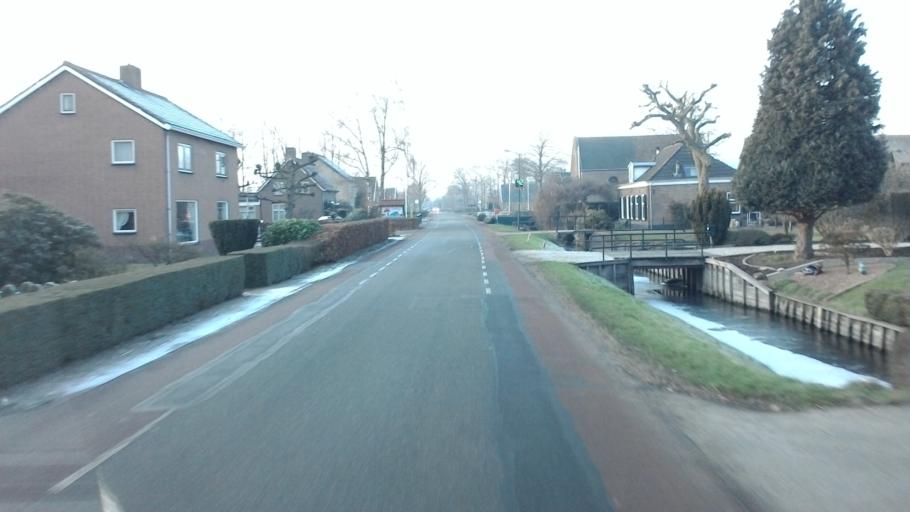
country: NL
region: North Holland
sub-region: Gemeente Wijdemeren
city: Nieuw-Loosdrecht
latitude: 52.1536
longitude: 5.1194
